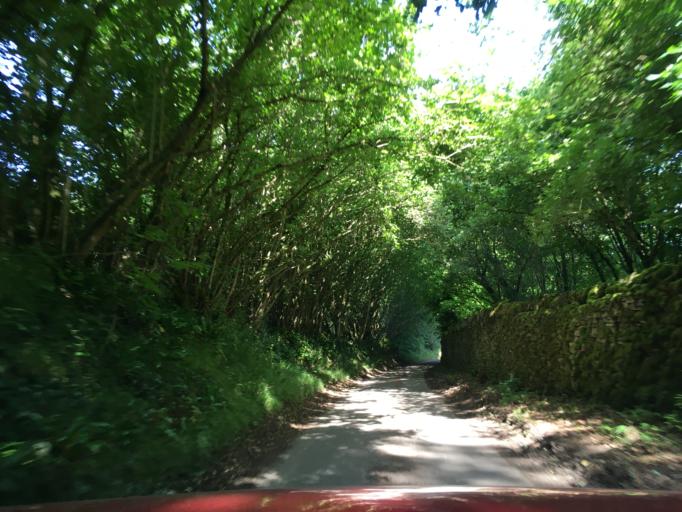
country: GB
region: England
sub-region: Wiltshire
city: Nettleton
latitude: 51.4932
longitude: -2.2701
